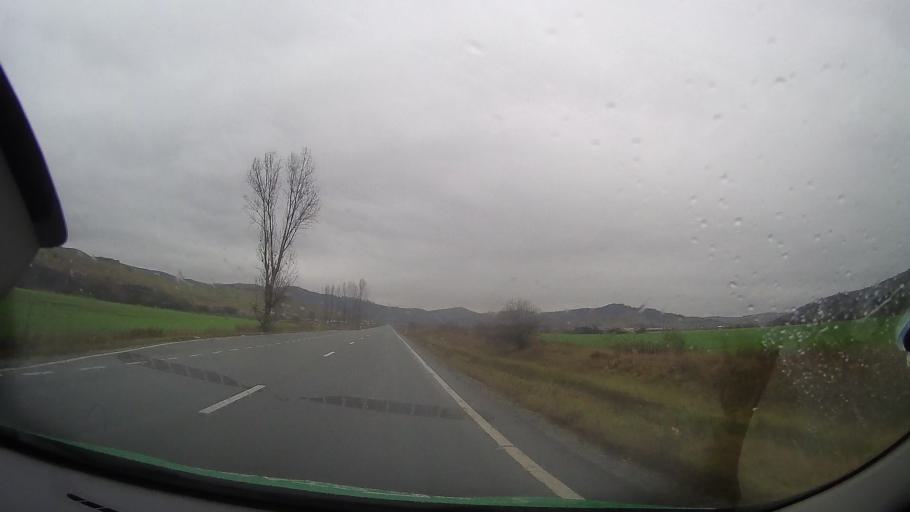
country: RO
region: Bistrita-Nasaud
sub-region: Comuna Teaca
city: Teaca
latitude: 46.9239
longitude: 24.4882
